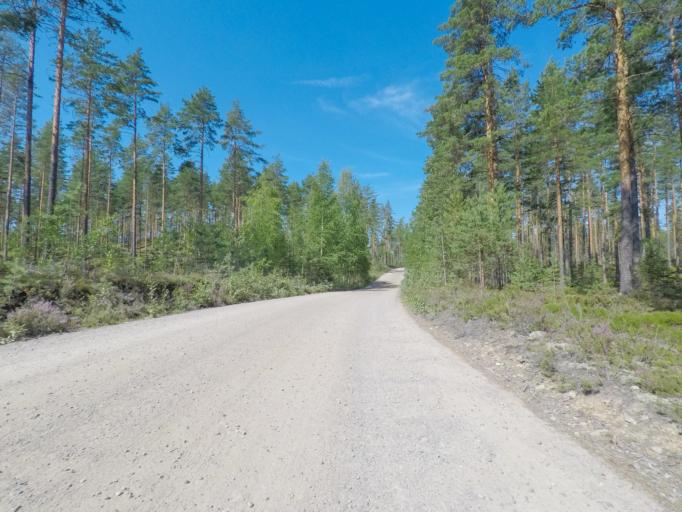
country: FI
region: Southern Savonia
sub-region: Mikkeli
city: Puumala
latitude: 61.4150
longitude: 28.0445
